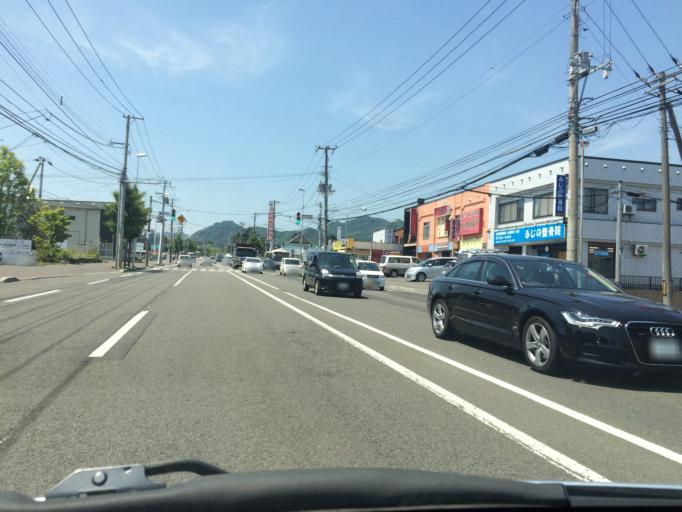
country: JP
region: Hokkaido
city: Sapporo
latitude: 42.9619
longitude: 141.2902
